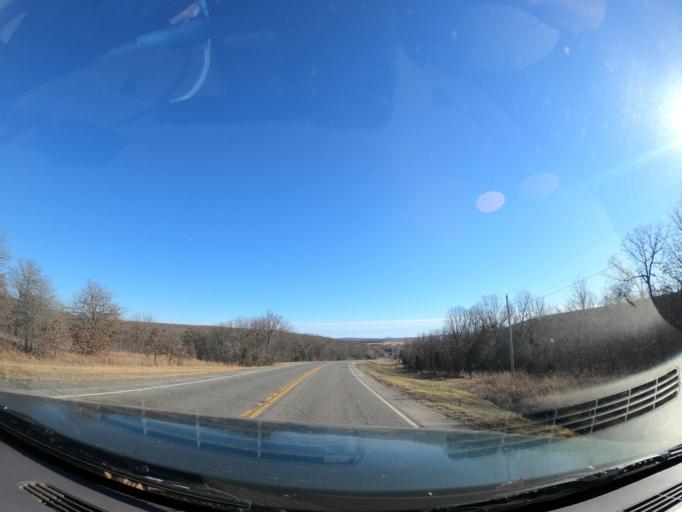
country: US
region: Oklahoma
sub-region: Pittsburg County
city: Longtown
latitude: 35.2227
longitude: -95.4307
